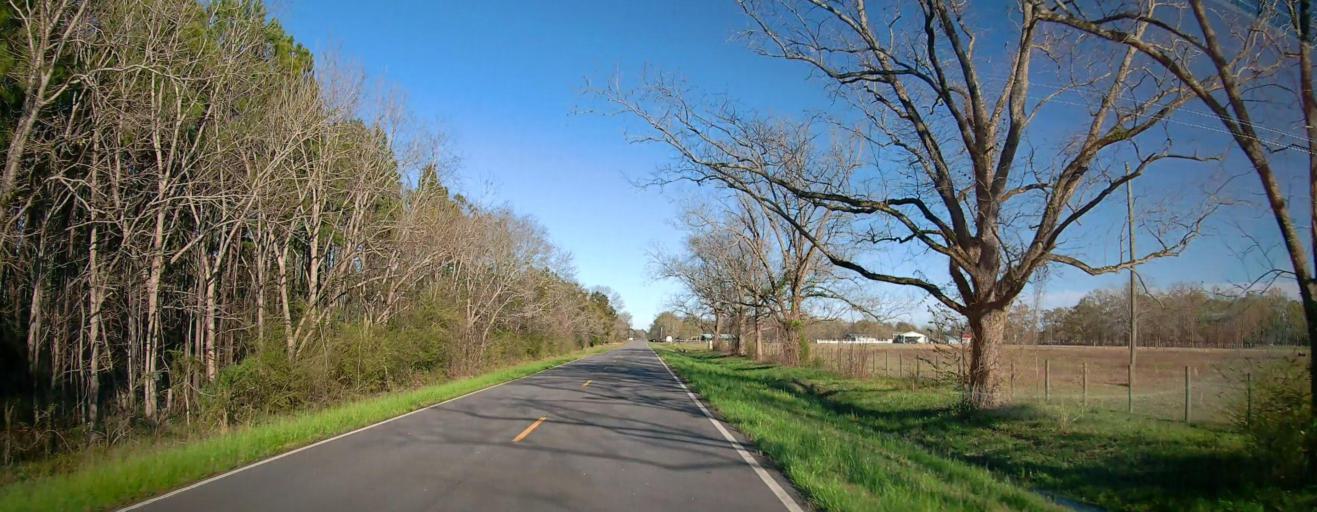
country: US
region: Georgia
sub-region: Pulaski County
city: Hawkinsville
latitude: 32.3479
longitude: -83.6026
